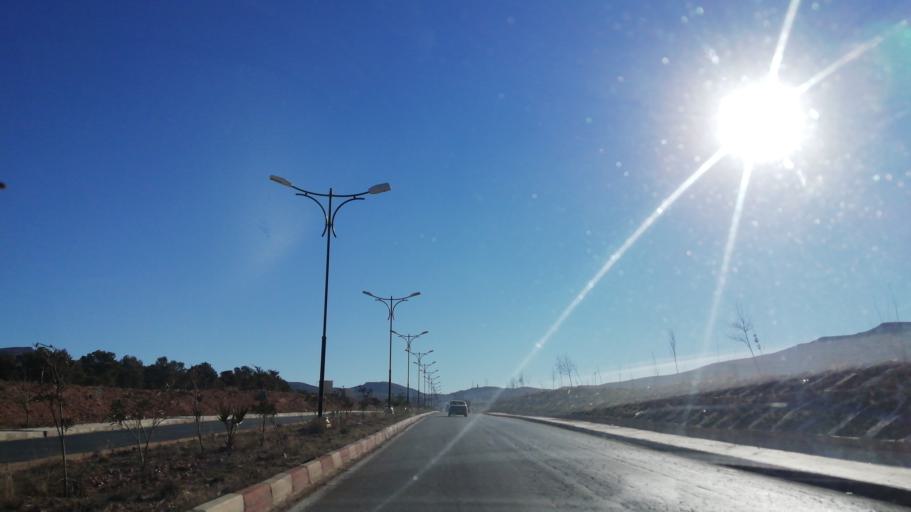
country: DZ
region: El Bayadh
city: El Bayadh
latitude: 33.6606
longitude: 1.0586
